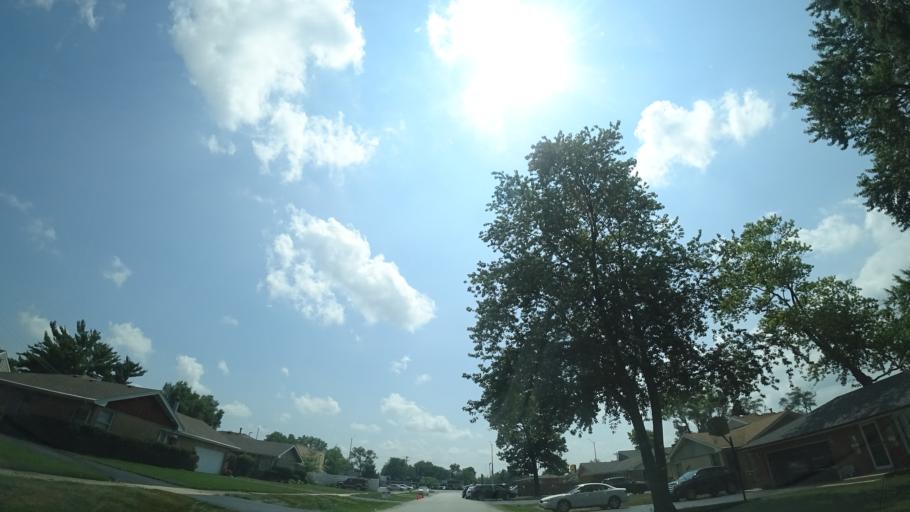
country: US
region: Illinois
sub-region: Cook County
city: Chicago Ridge
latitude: 41.6916
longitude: -87.7813
